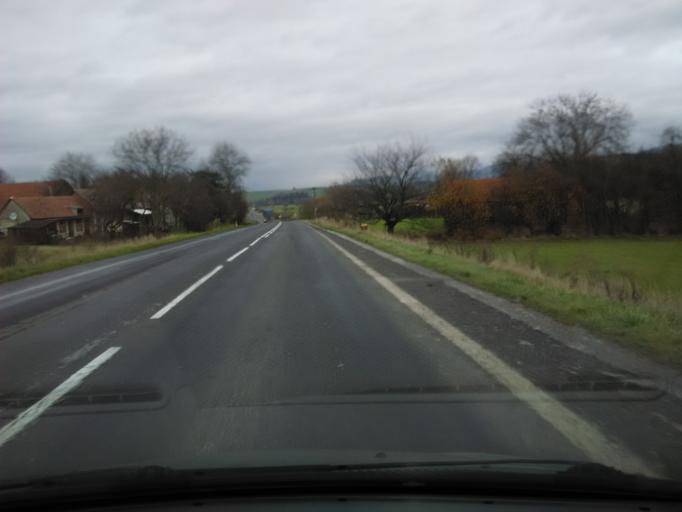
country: SK
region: Zilinsky
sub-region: Okres Martin
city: Martin
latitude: 48.9578
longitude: 18.9009
